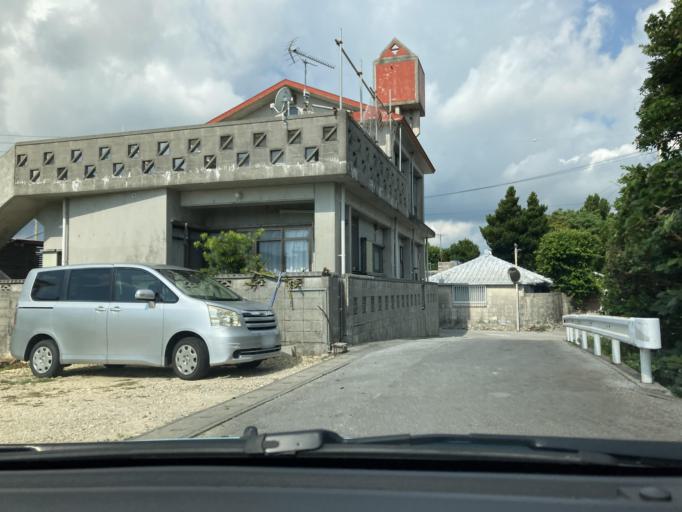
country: JP
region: Okinawa
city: Itoman
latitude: 26.1302
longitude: 127.7727
